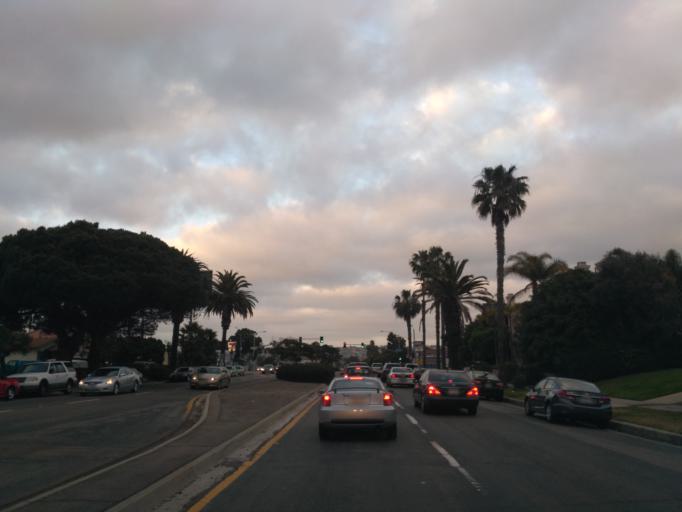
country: US
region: California
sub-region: San Diego County
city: La Jolla
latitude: 32.7987
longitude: -117.2363
